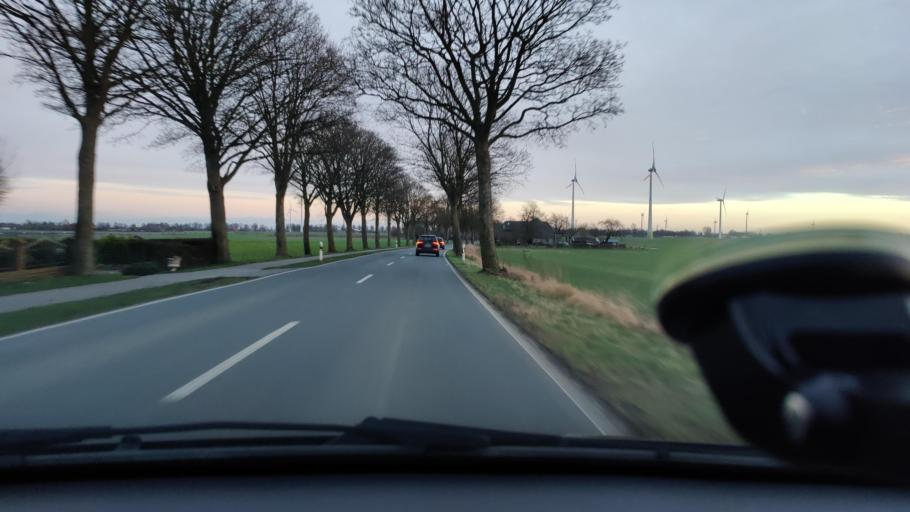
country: DE
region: North Rhine-Westphalia
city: Kalkar
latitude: 51.7176
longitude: 6.2237
